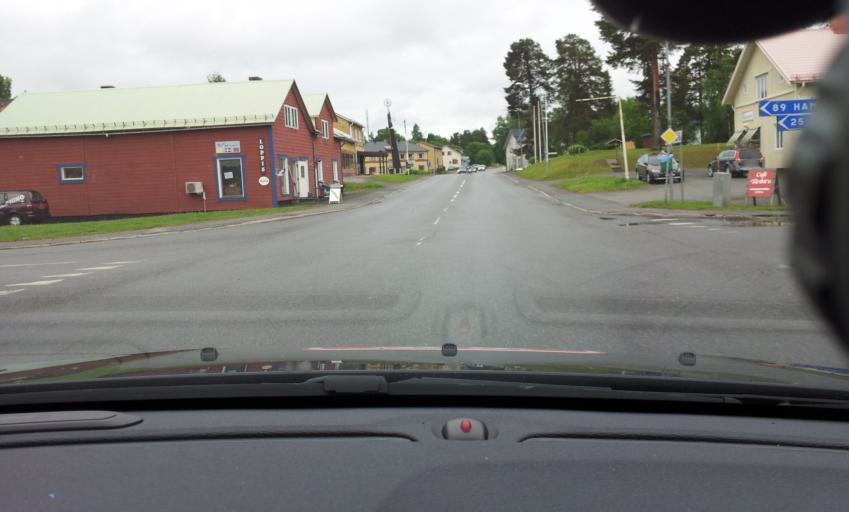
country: SE
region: Jaemtland
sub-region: Stroemsunds Kommun
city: Stroemsund
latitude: 63.5821
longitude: 15.3518
